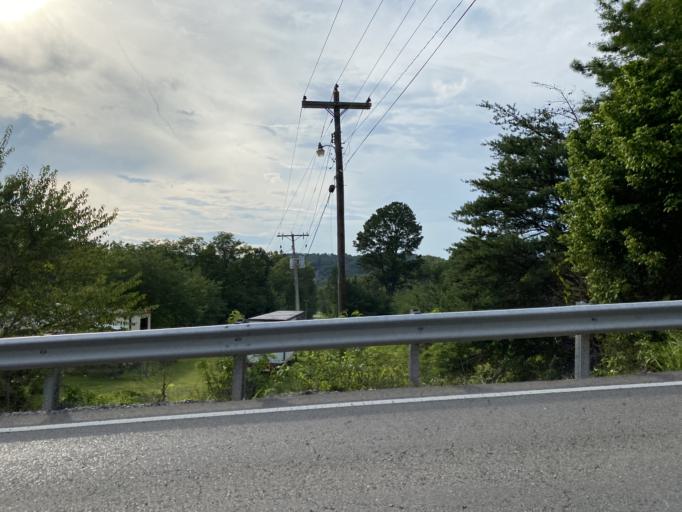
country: US
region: Alabama
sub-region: DeKalb County
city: Fort Payne
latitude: 34.4447
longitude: -85.7107
